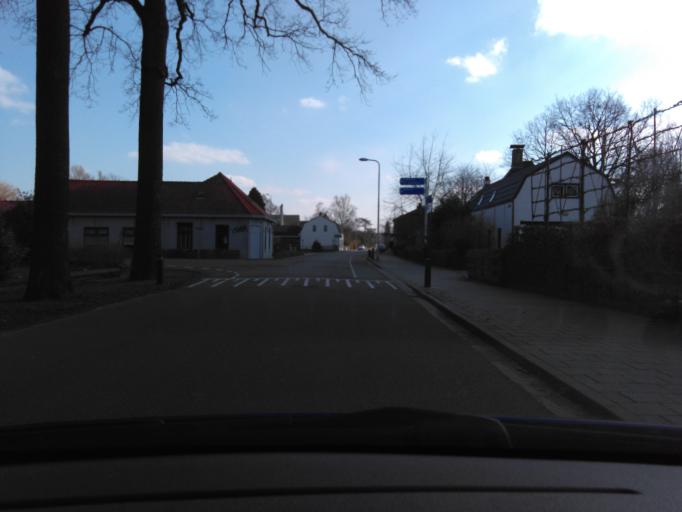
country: NL
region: Zeeland
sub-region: Gemeente Terneuzen
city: Koewacht
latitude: 51.2304
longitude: 3.9668
